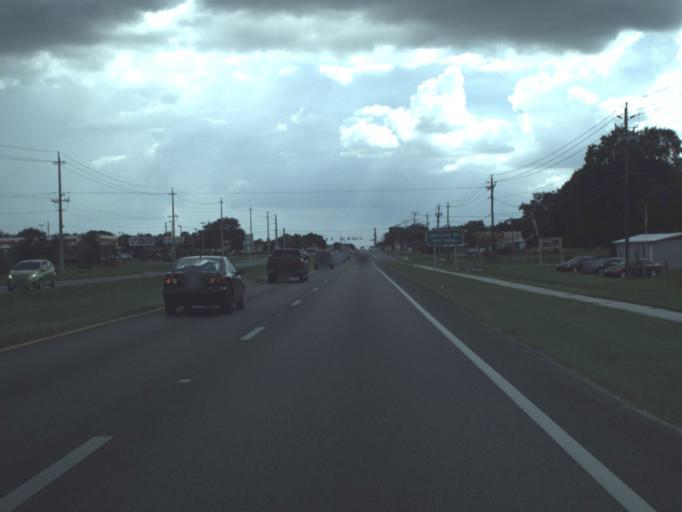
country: US
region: Florida
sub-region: Polk County
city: Gibsonia
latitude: 28.1330
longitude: -81.9737
